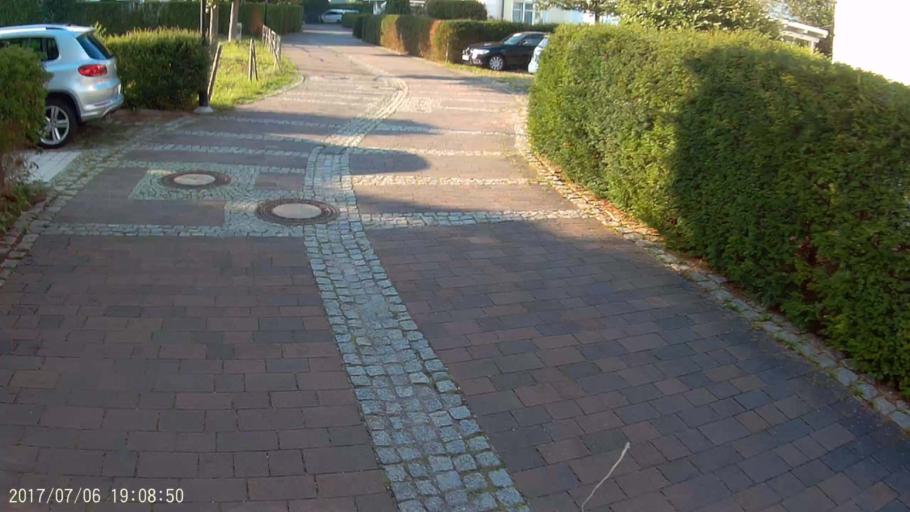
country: DE
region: Brandenburg
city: Hohen Neuendorf
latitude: 52.6535
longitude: 13.2535
